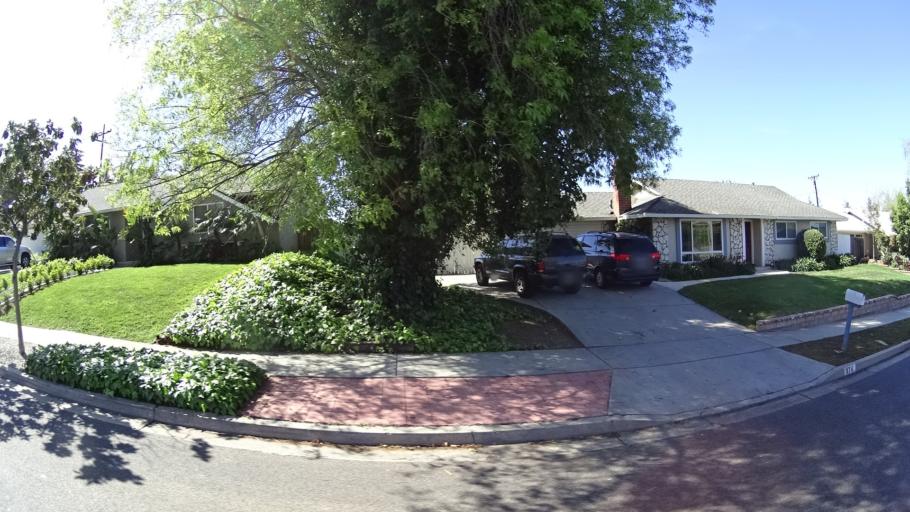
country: US
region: California
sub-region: Ventura County
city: Thousand Oaks
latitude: 34.2189
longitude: -118.8633
